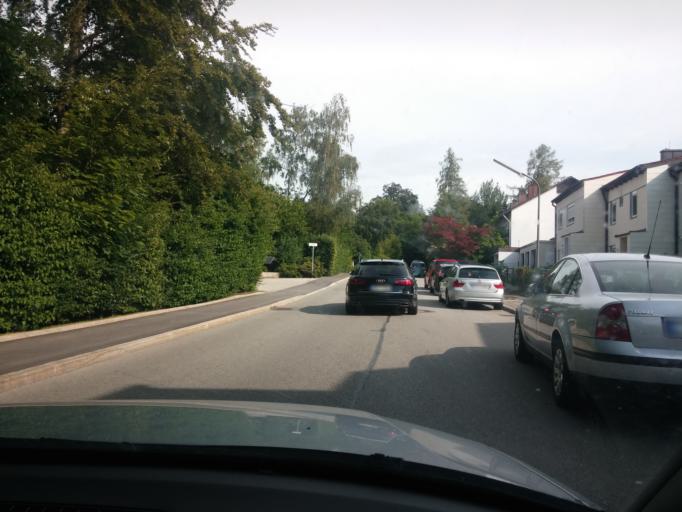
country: DE
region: Bavaria
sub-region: Upper Bavaria
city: Kirchseeon
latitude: 48.0647
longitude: 11.8921
